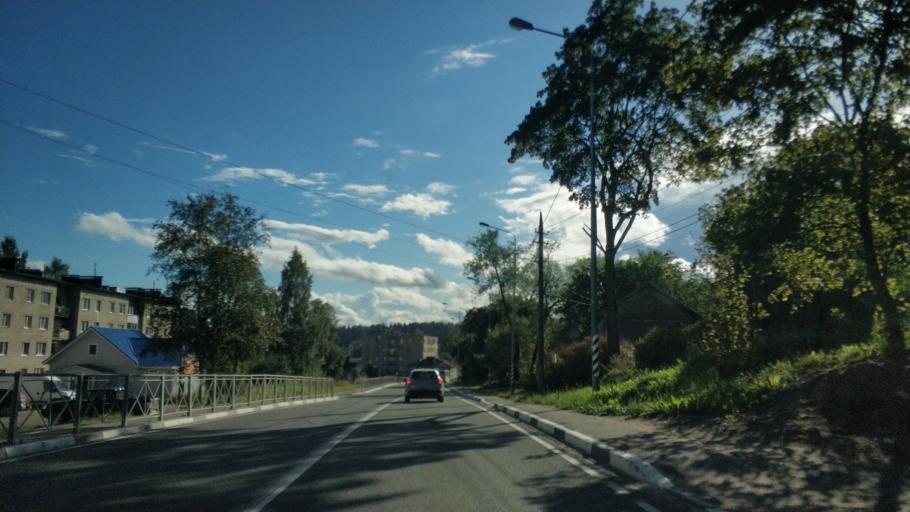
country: RU
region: Republic of Karelia
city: Lakhdenpokh'ya
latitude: 61.5234
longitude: 30.1990
